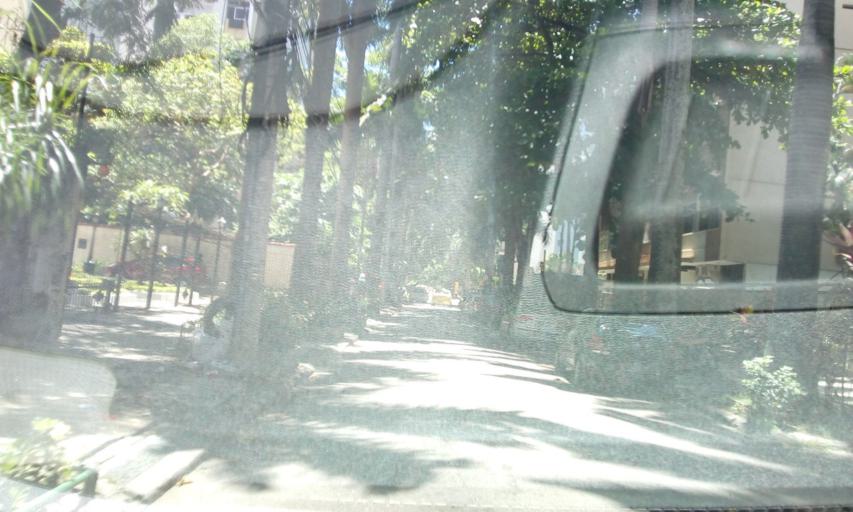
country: BR
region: Rio de Janeiro
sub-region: Rio De Janeiro
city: Rio de Janeiro
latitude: -22.9353
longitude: -43.1793
